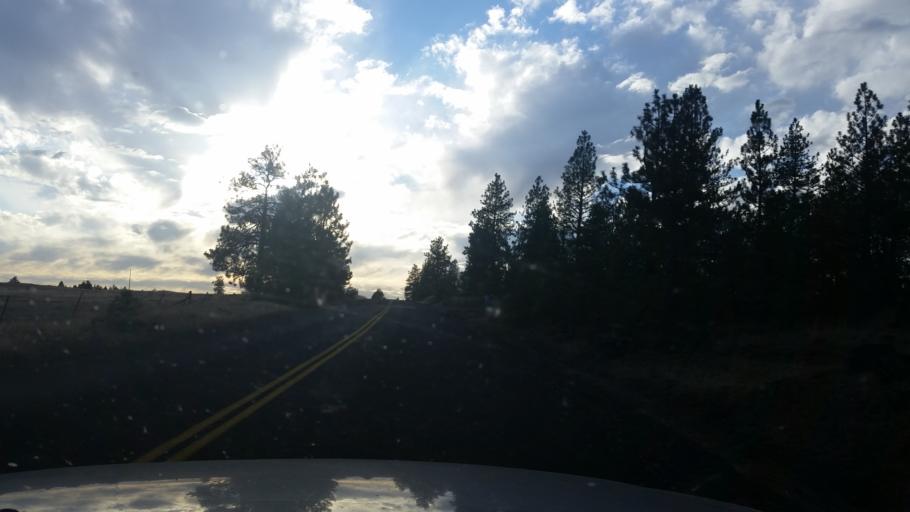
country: US
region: Washington
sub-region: Spokane County
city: Medical Lake
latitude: 47.4534
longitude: -117.8048
